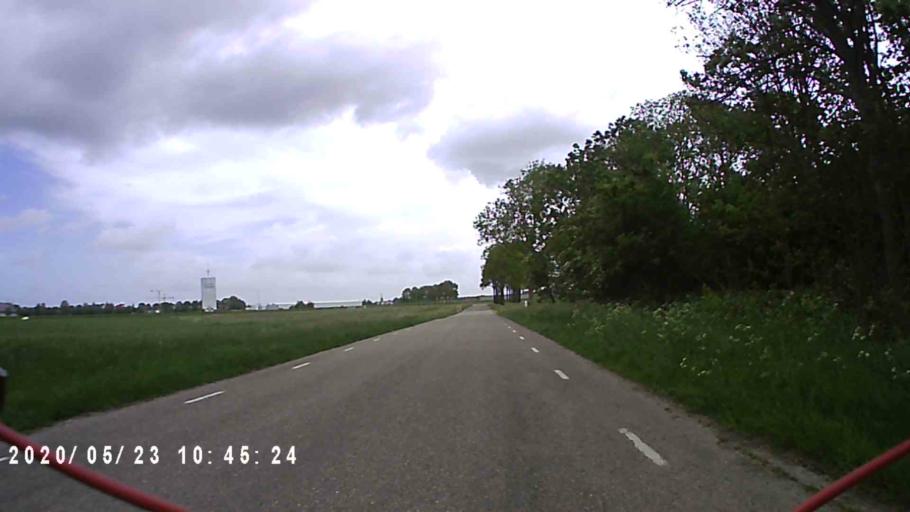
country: NL
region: Groningen
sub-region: Gemeente Delfzijl
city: Delfzijl
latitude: 53.3086
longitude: 6.9164
